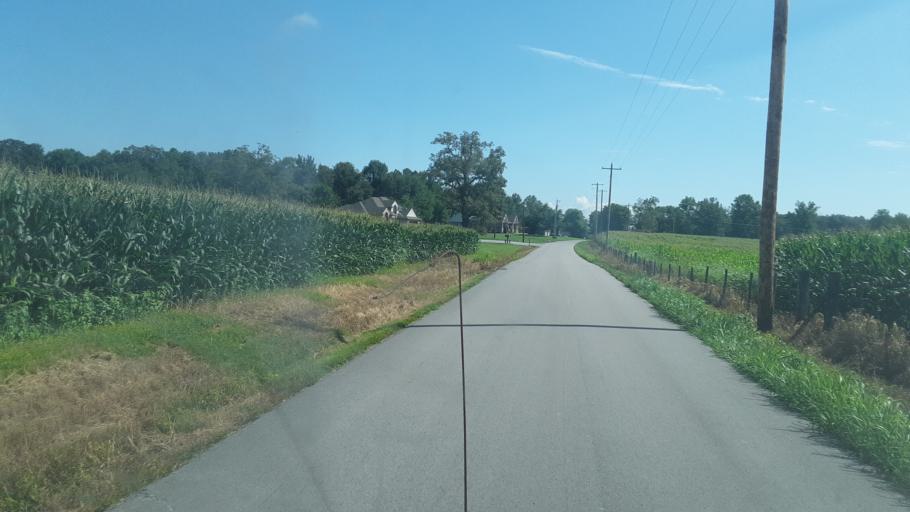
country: US
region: Kentucky
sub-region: Todd County
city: Elkton
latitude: 36.7936
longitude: -87.2047
